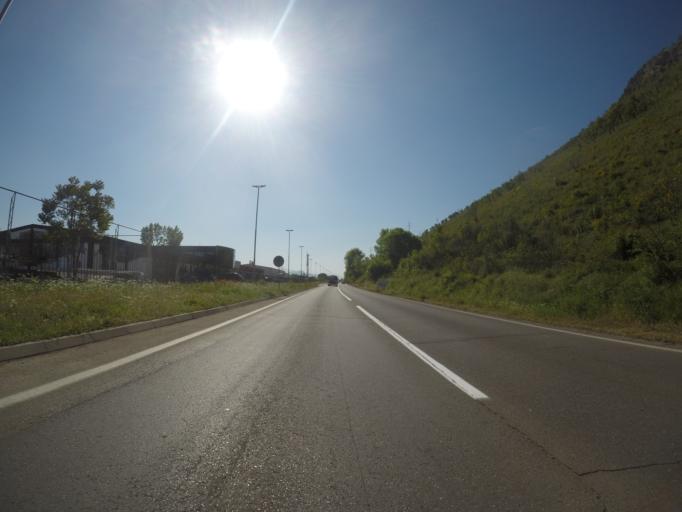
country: ME
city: Spuz
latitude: 42.4528
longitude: 19.1950
